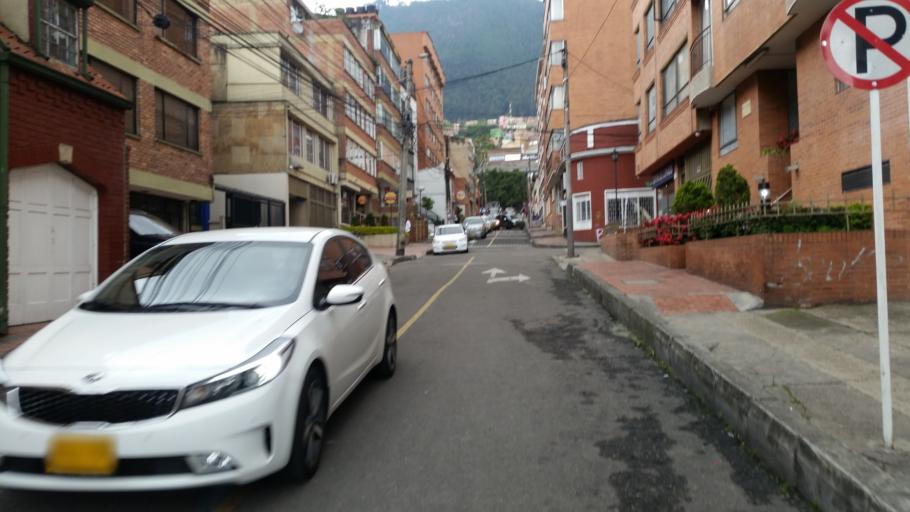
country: CO
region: Bogota D.C.
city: Bogota
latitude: 4.6313
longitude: -74.0658
